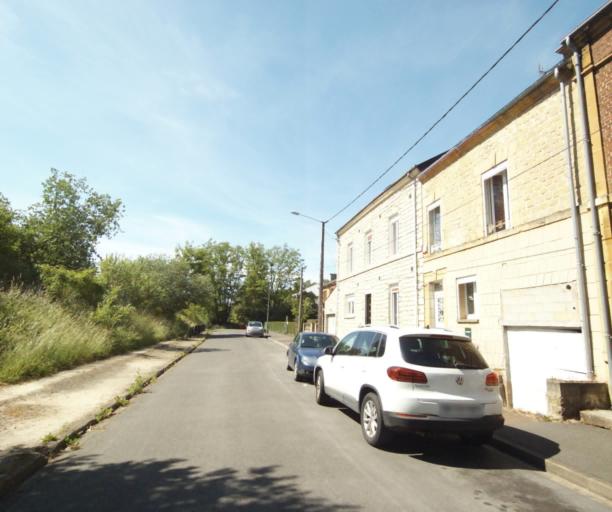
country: FR
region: Champagne-Ardenne
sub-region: Departement des Ardennes
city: Villers-Semeuse
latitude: 49.7438
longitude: 4.7341
